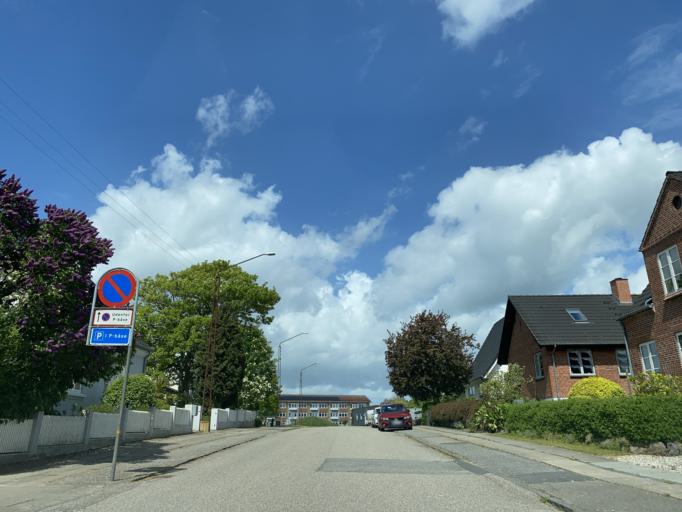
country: DK
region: South Denmark
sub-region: Sonderborg Kommune
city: Sonderborg
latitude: 54.9139
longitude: 9.8059
